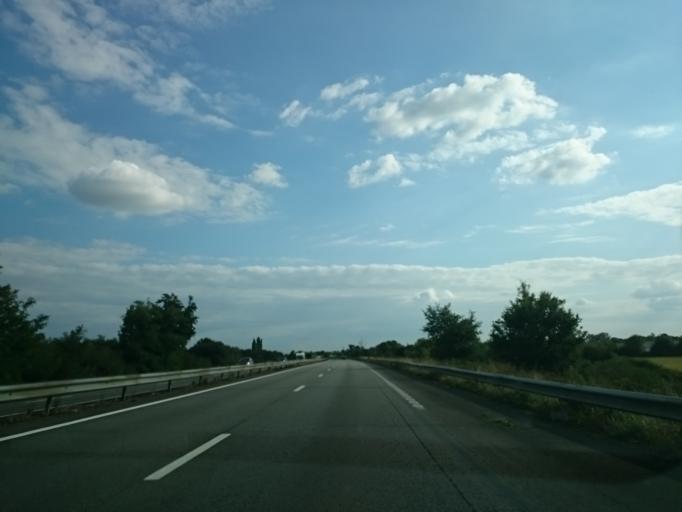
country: FR
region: Pays de la Loire
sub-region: Departement de la Loire-Atlantique
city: Heric
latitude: 47.4562
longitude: -1.6403
